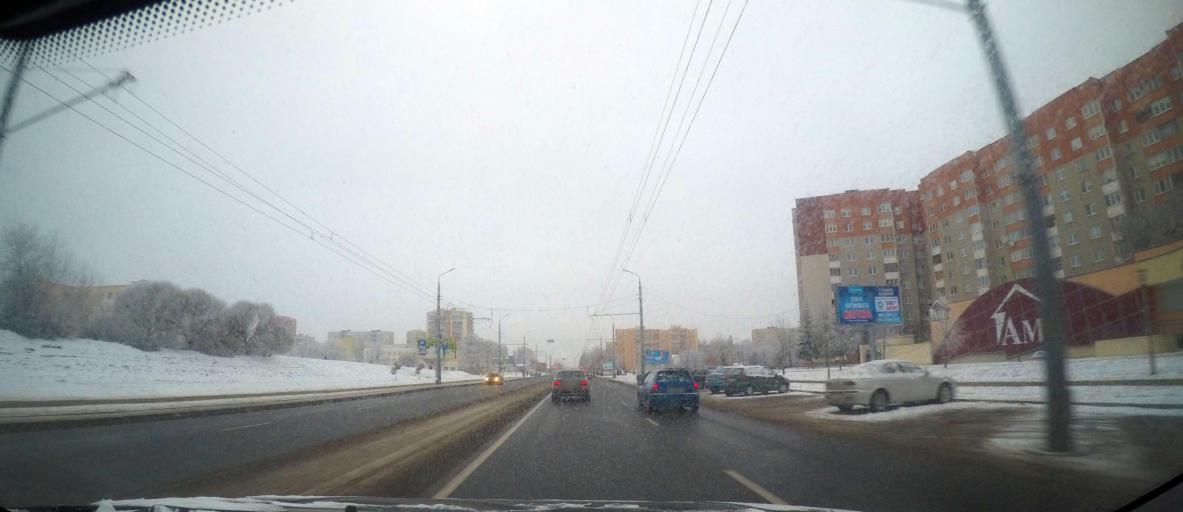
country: BY
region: Grodnenskaya
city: Hrodna
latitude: 53.6555
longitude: 23.8461
